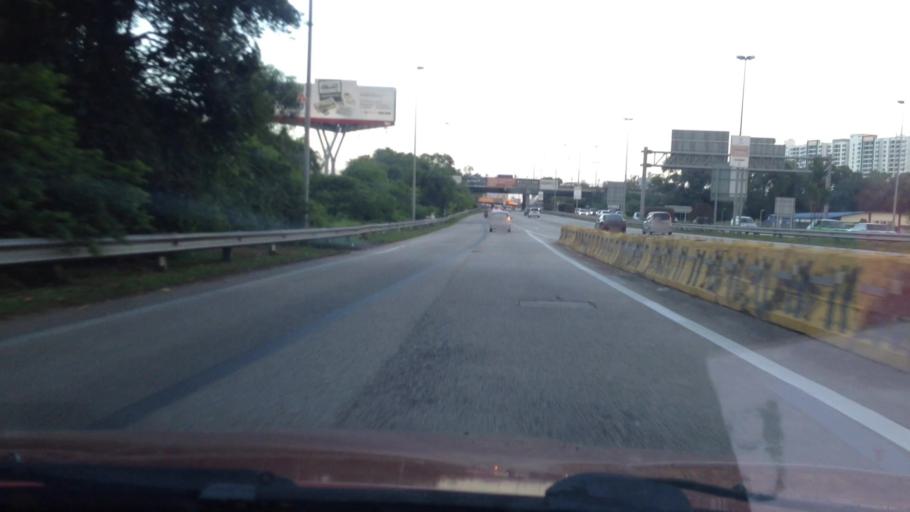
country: MY
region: Selangor
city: Shah Alam
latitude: 3.0970
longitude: 101.5489
